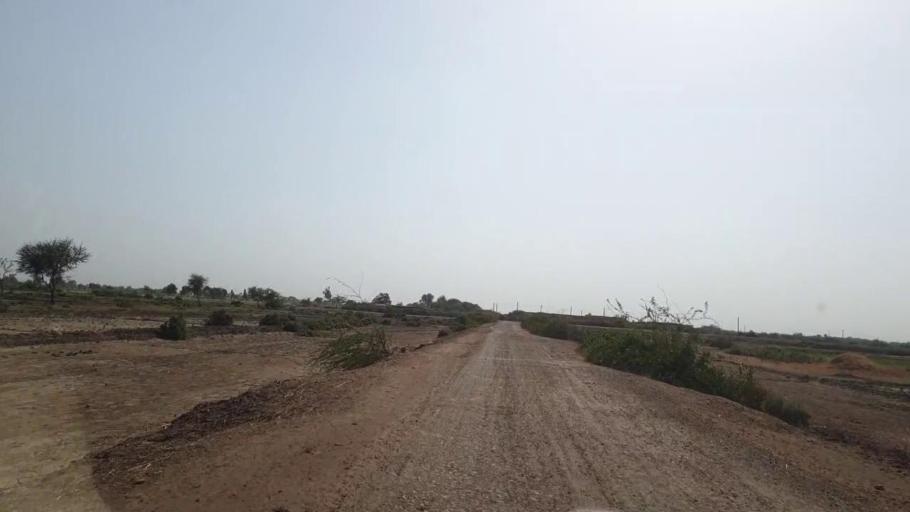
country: PK
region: Sindh
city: Rajo Khanani
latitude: 25.0422
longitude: 68.8511
